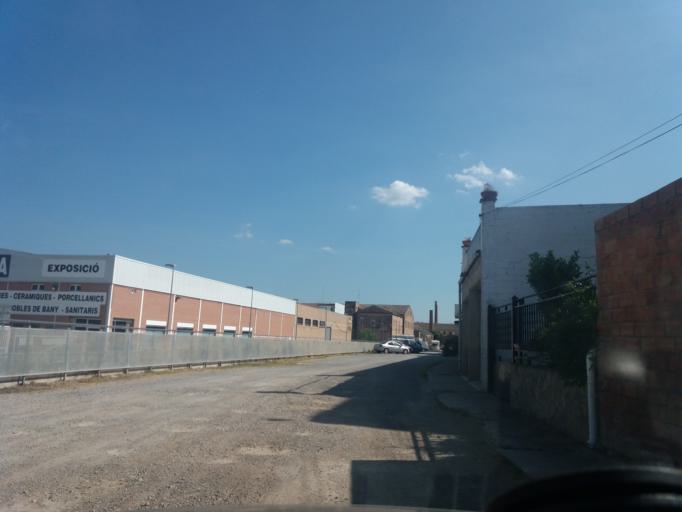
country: ES
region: Catalonia
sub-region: Provincia de Barcelona
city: Sant Joan de Vilatorrada
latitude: 41.7468
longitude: 1.8081
